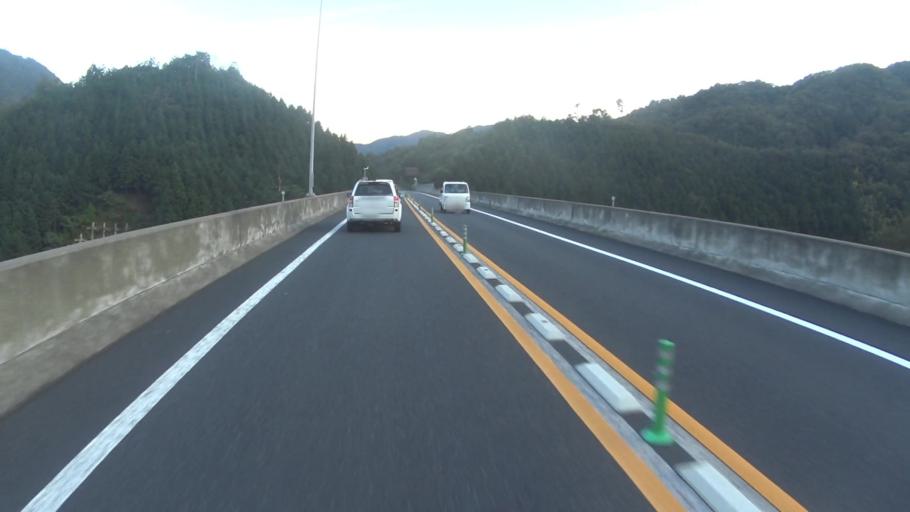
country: JP
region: Kyoto
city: Miyazu
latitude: 35.4550
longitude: 135.1783
